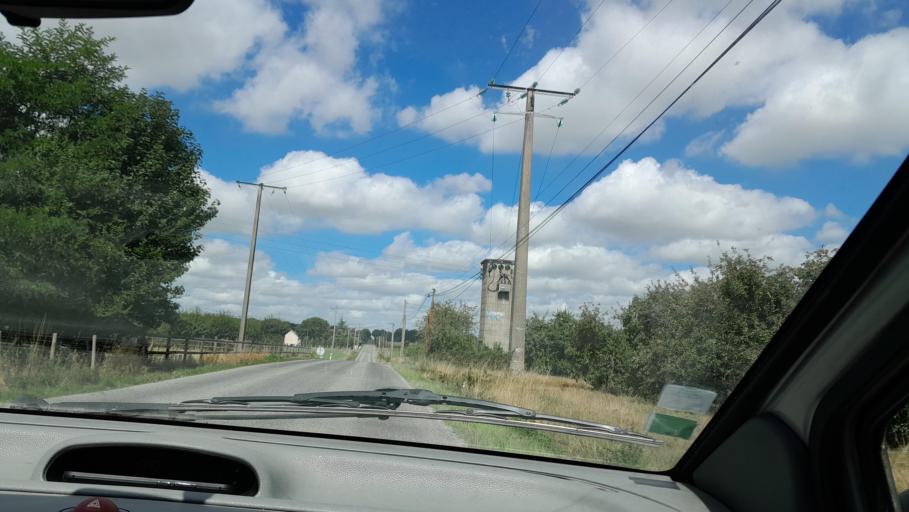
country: FR
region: Pays de la Loire
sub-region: Departement de la Mayenne
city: Ballots
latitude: 47.8784
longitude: -1.0151
